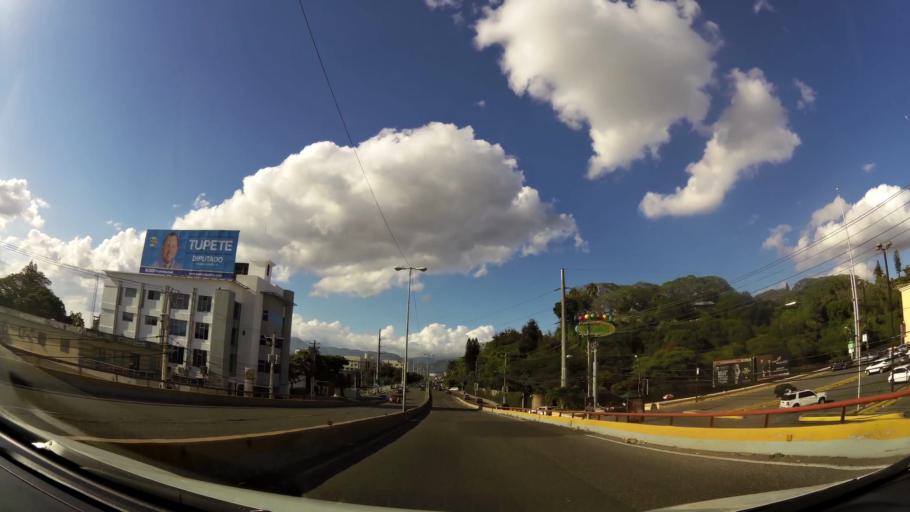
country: DO
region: Santiago
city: Santiago de los Caballeros
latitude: 19.4617
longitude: -70.6863
